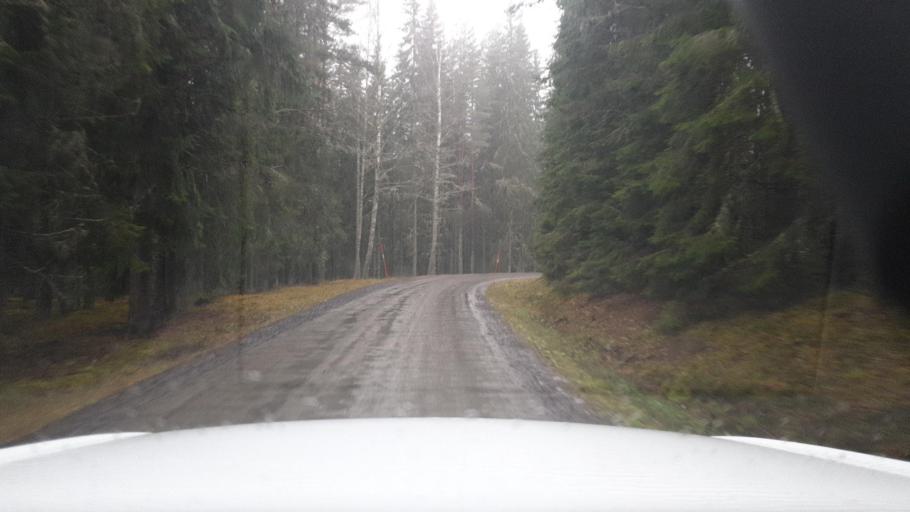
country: SE
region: Vaermland
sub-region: Sunne Kommun
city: Sunne
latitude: 59.8553
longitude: 12.9252
